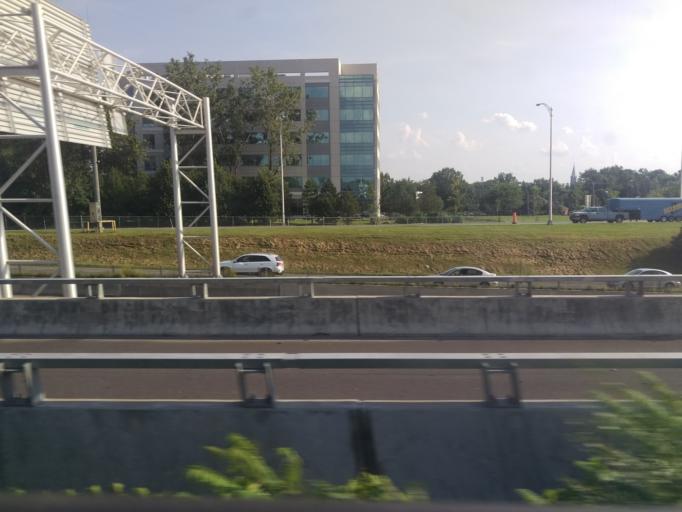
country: CA
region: Quebec
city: Dorval
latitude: 45.4489
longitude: -73.7336
